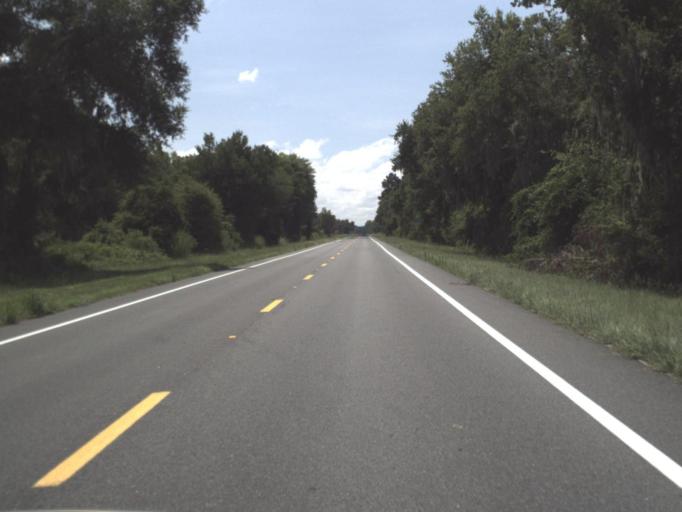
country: US
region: Florida
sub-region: Hamilton County
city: Jasper
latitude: 30.4059
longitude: -82.8410
